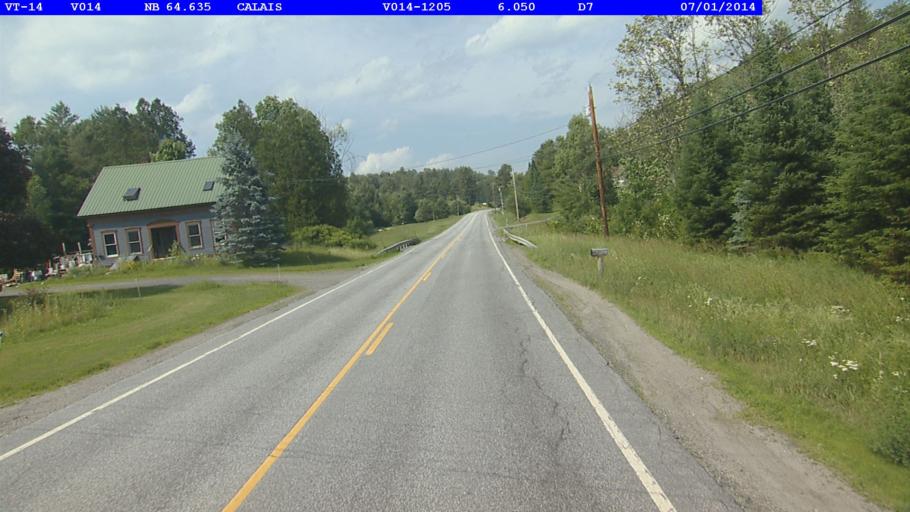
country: US
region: Vermont
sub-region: Caledonia County
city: Hardwick
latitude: 44.3844
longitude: -72.4178
